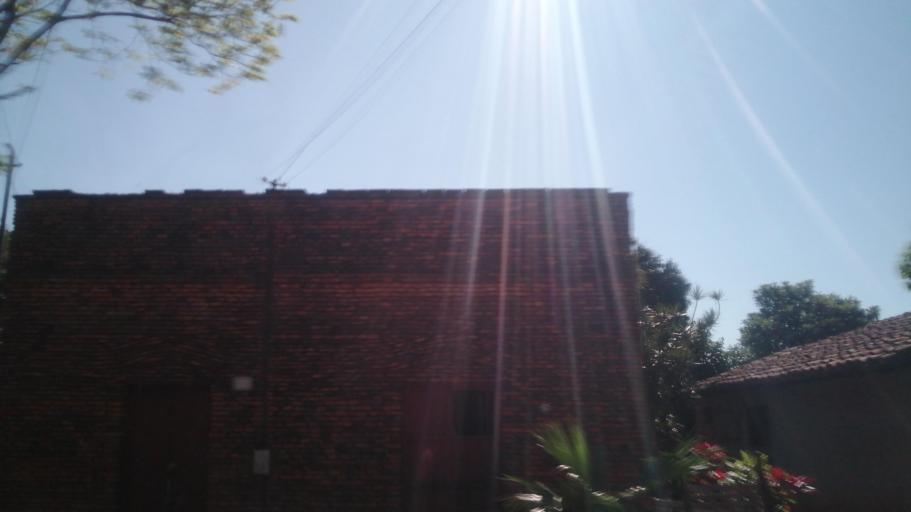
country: PY
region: Misiones
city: San Juan Bautista
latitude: -26.6655
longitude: -57.1471
